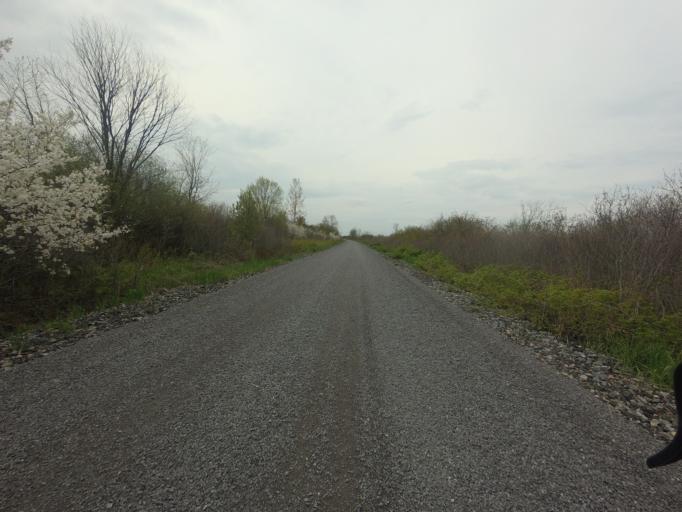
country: CA
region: Ontario
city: Carleton Place
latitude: 45.2018
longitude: -76.1683
